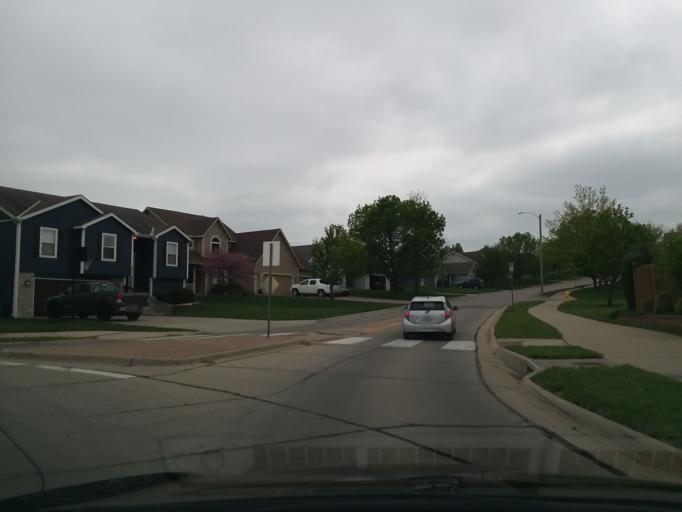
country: US
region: Kansas
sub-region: Douglas County
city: Lawrence
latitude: 38.9902
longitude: -95.2793
